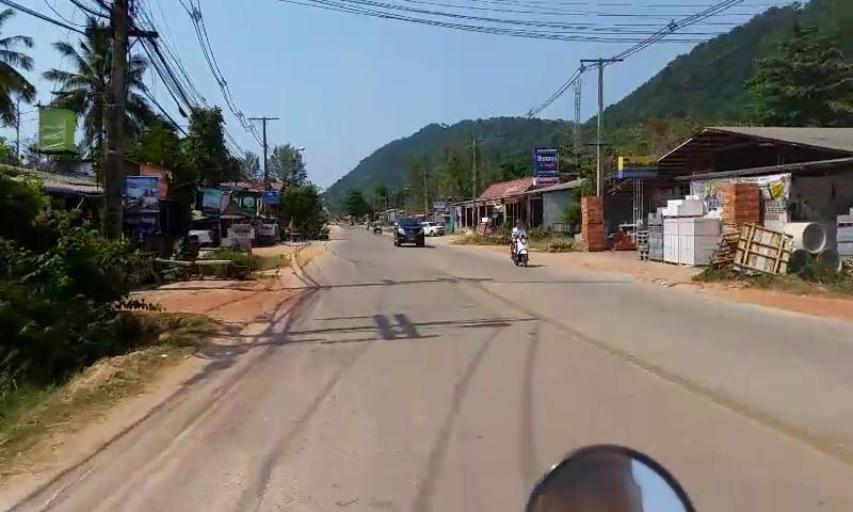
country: TH
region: Krabi
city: Saladan
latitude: 7.6237
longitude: 99.0330
